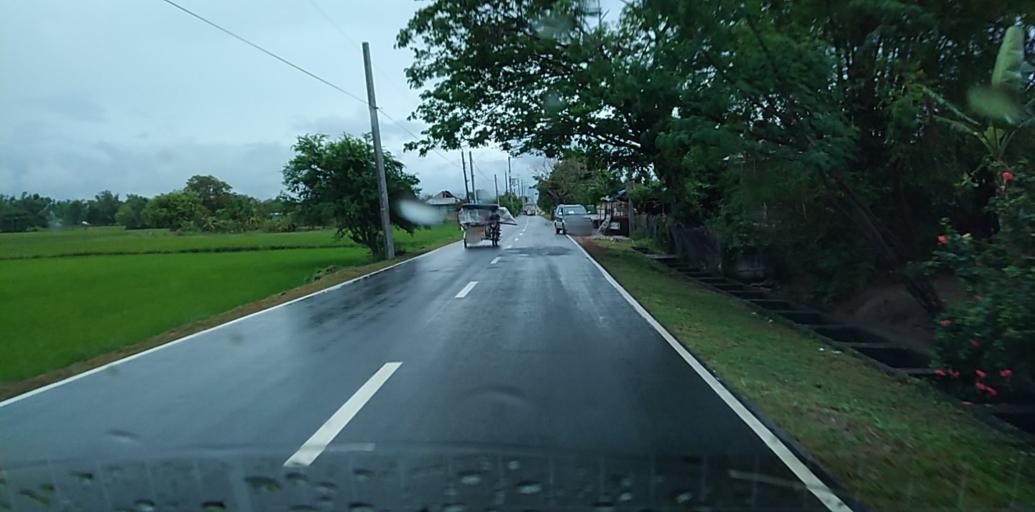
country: PH
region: Central Luzon
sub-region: Province of Pampanga
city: Salapungan
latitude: 15.1352
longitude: 120.9179
